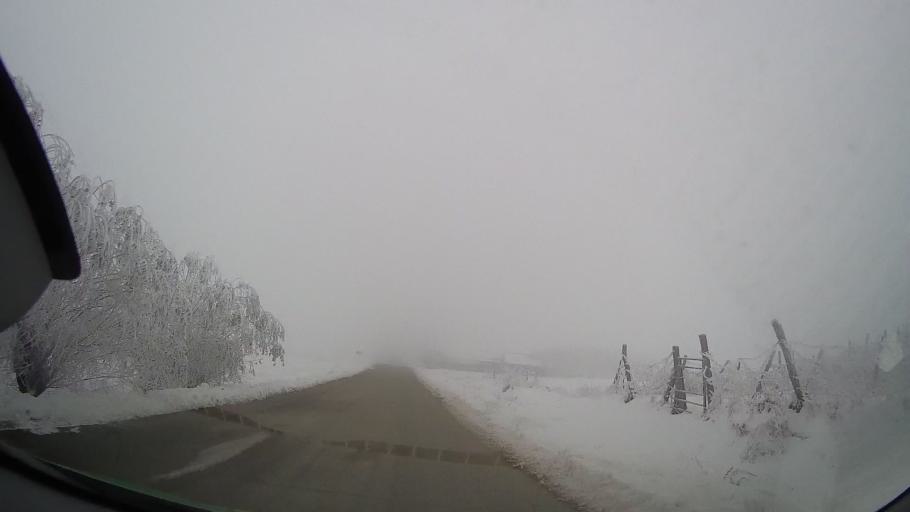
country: RO
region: Iasi
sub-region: Comuna Tansa
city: Suhulet
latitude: 46.8938
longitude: 27.2677
